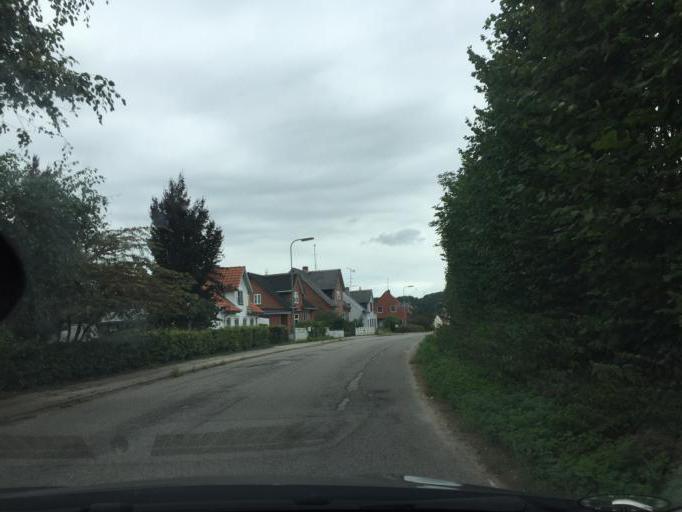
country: DK
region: South Denmark
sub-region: Assens Kommune
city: Vissenbjerg
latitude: 55.3764
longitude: 10.1013
